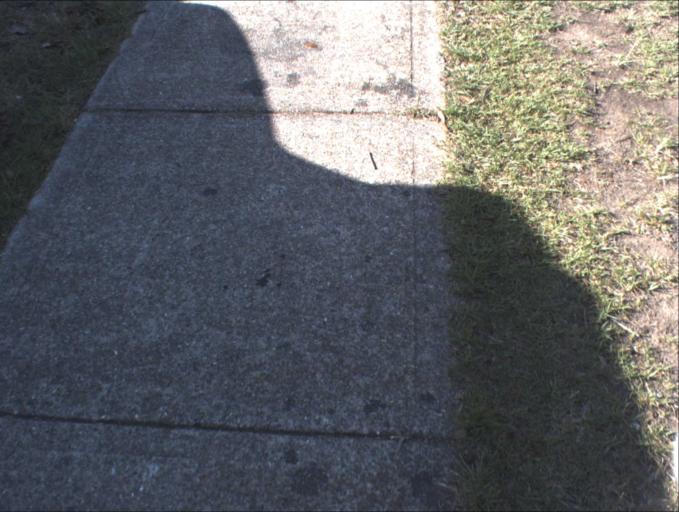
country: AU
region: Queensland
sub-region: Gold Coast
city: Yatala
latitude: -27.7016
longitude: 153.2180
